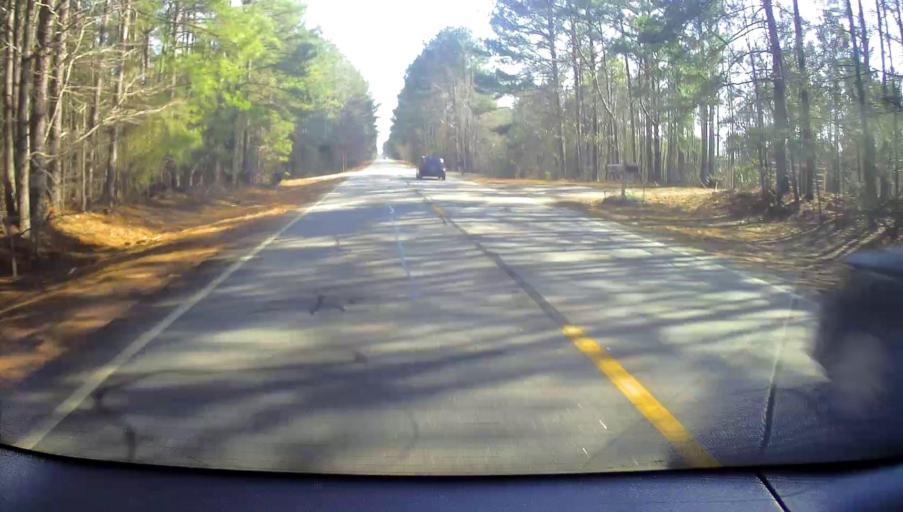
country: US
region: Georgia
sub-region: Butts County
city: Indian Springs
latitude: 33.2413
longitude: -83.8826
